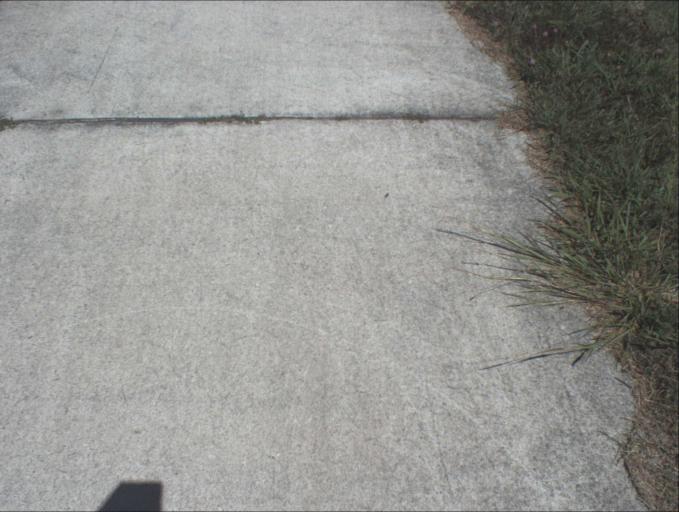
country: AU
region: Queensland
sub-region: Logan
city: Windaroo
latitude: -27.7588
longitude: 153.1883
